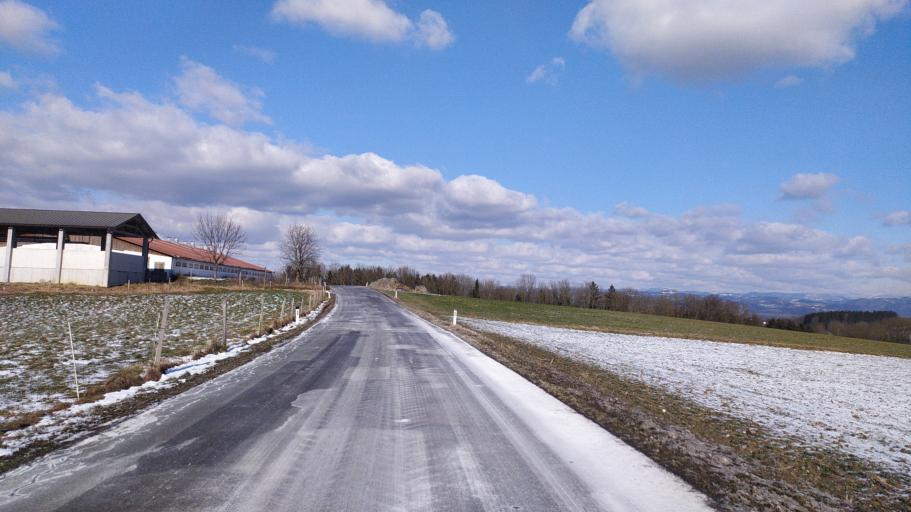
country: AT
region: Lower Austria
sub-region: Politischer Bezirk Amstetten
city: Zeillern
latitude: 48.1362
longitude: 14.7397
